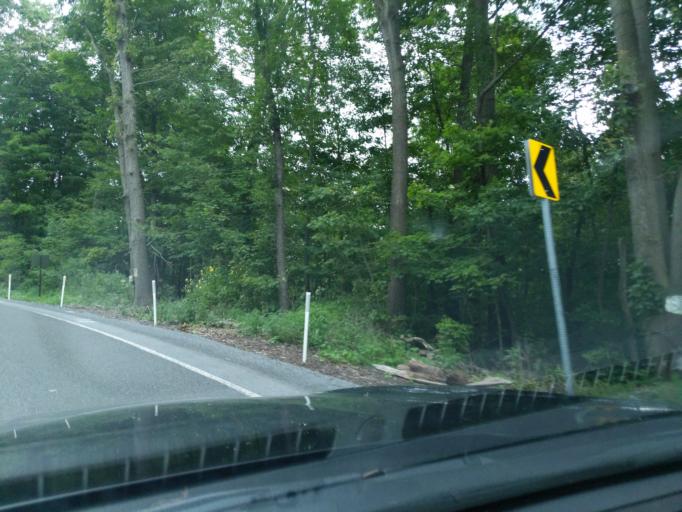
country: US
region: Pennsylvania
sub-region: Blair County
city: Claysburg
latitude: 40.3553
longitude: -78.5136
